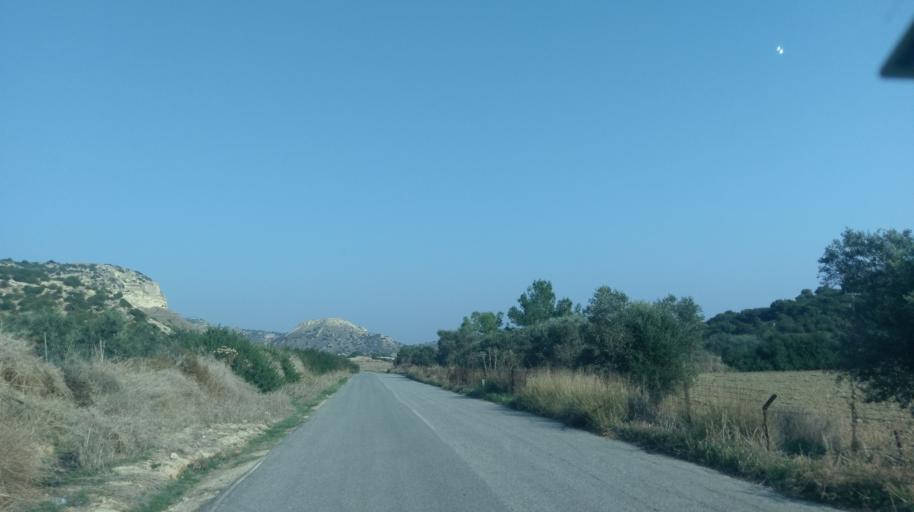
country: CY
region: Ammochostos
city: Rizokarpaso
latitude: 35.5134
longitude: 34.2896
